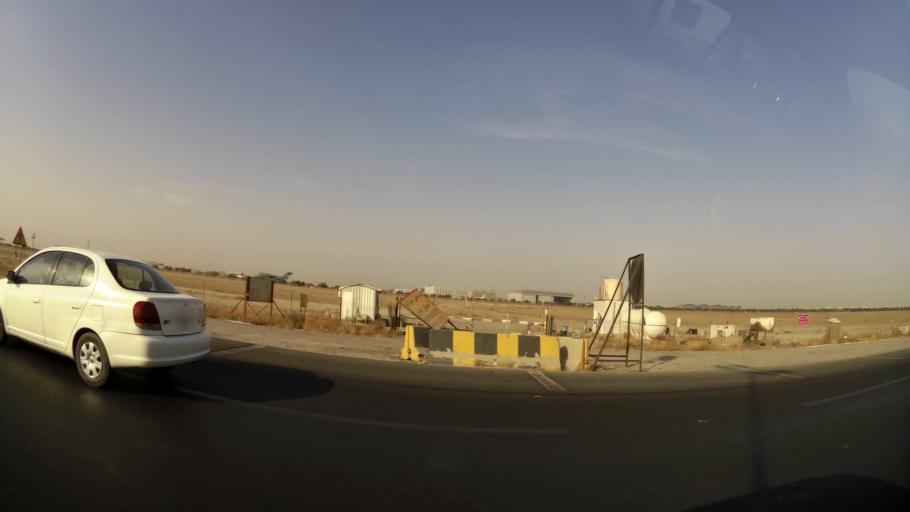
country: KW
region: Al Farwaniyah
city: Janub as Surrah
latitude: 29.2410
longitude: 47.9912
